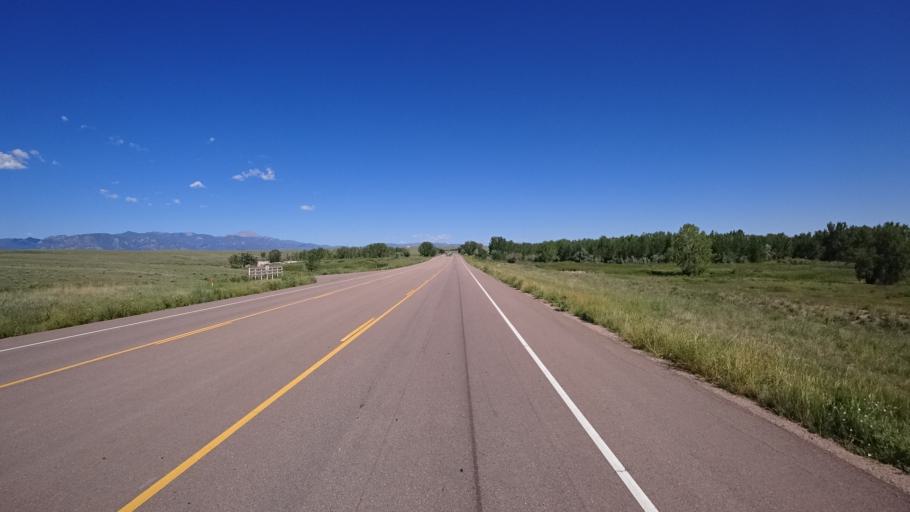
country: US
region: Colorado
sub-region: El Paso County
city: Security-Widefield
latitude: 38.7495
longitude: -104.6513
